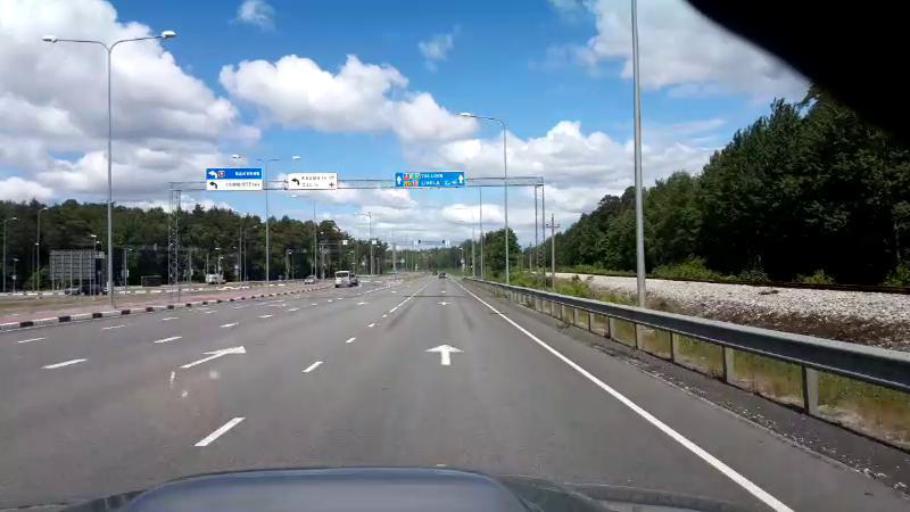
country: EE
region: Paernumaa
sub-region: Paernu linn
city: Parnu
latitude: 58.3820
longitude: 24.5566
